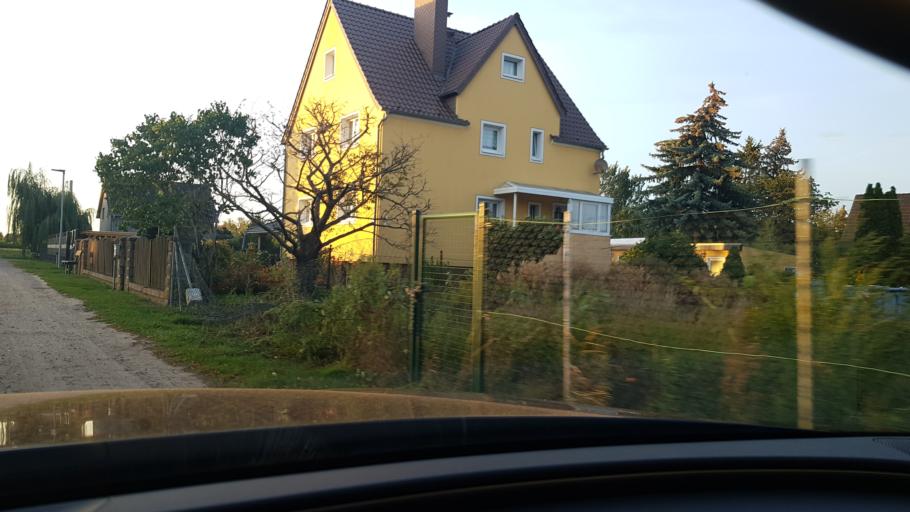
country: DE
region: Brandenburg
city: Brieselang
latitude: 52.5814
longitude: 12.9827
